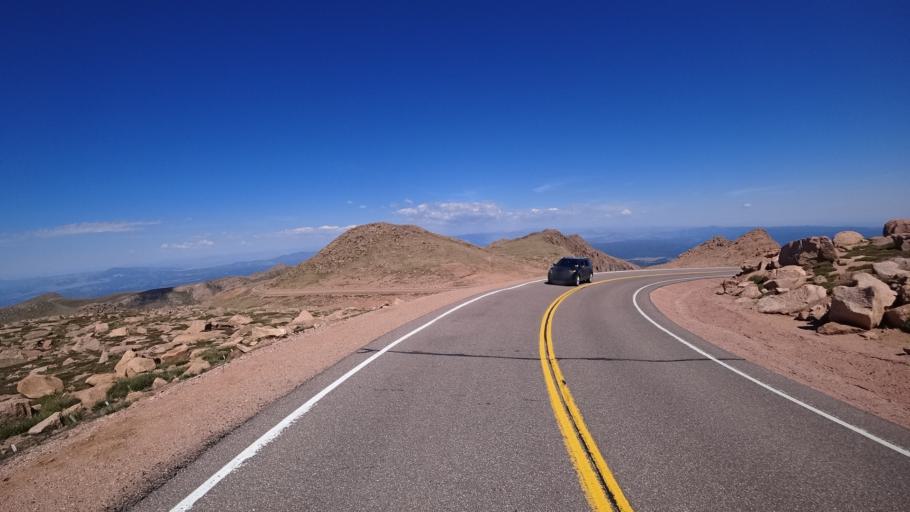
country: US
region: Colorado
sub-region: El Paso County
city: Cascade-Chipita Park
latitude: 38.8467
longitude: -105.0546
